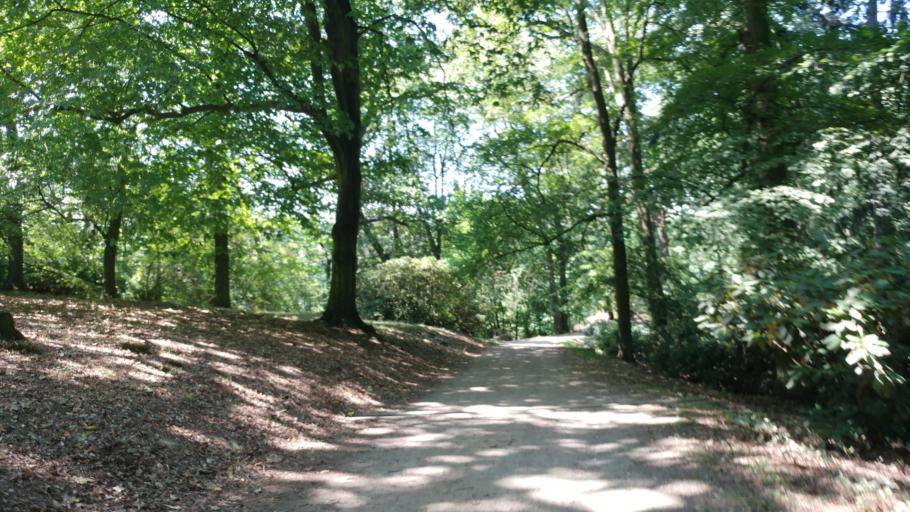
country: CZ
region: Central Bohemia
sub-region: Okres Praha-Zapad
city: Pruhonice
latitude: 49.9951
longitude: 14.5606
